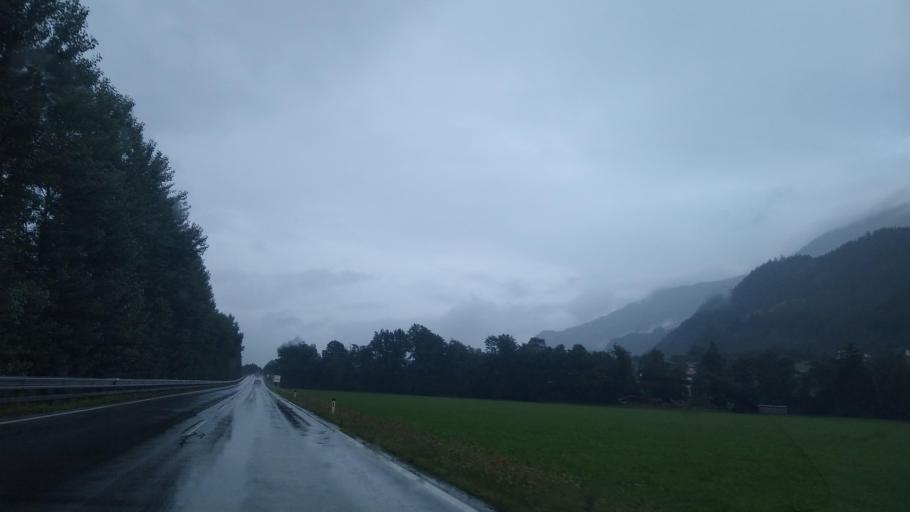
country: AT
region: Tyrol
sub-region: Politischer Bezirk Schwaz
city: Buch bei Jenbach
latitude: 47.3722
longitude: 11.7441
